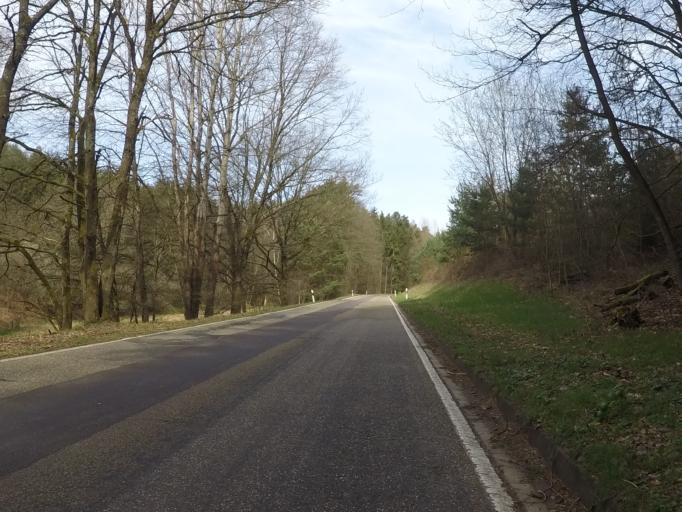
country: DE
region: Rheinland-Pfalz
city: Schwanheim
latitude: 49.1827
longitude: 7.8829
